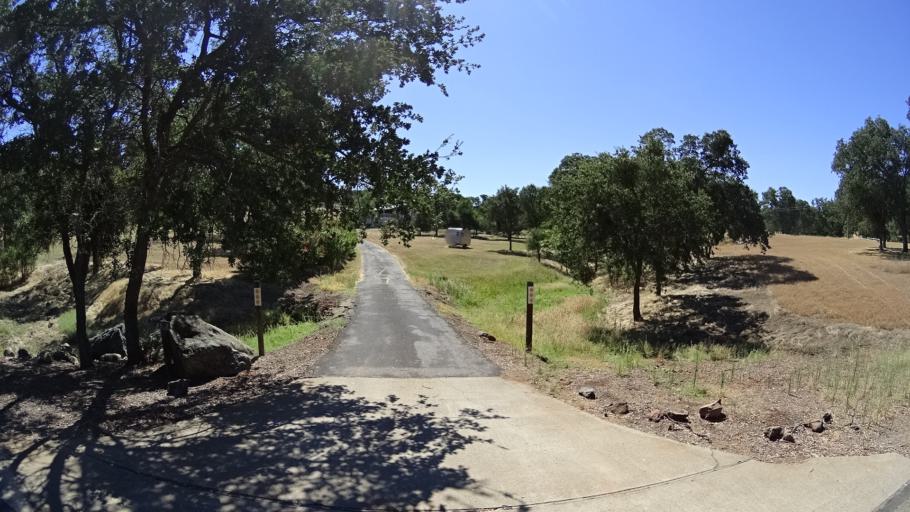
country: US
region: California
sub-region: Calaveras County
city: Rancho Calaveras
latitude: 38.1383
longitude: -120.8507
